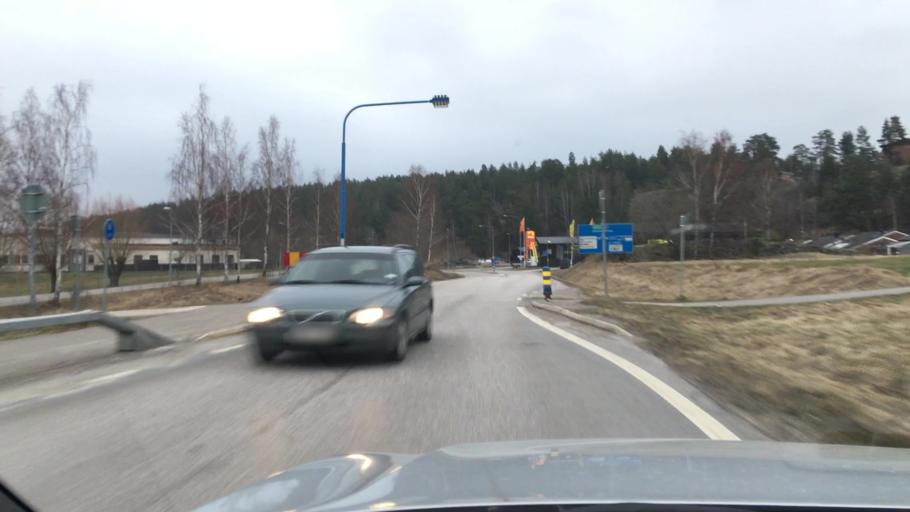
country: SE
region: OEstergoetland
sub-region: Valdemarsviks Kommun
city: Valdemarsvik
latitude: 58.2096
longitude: 16.5839
